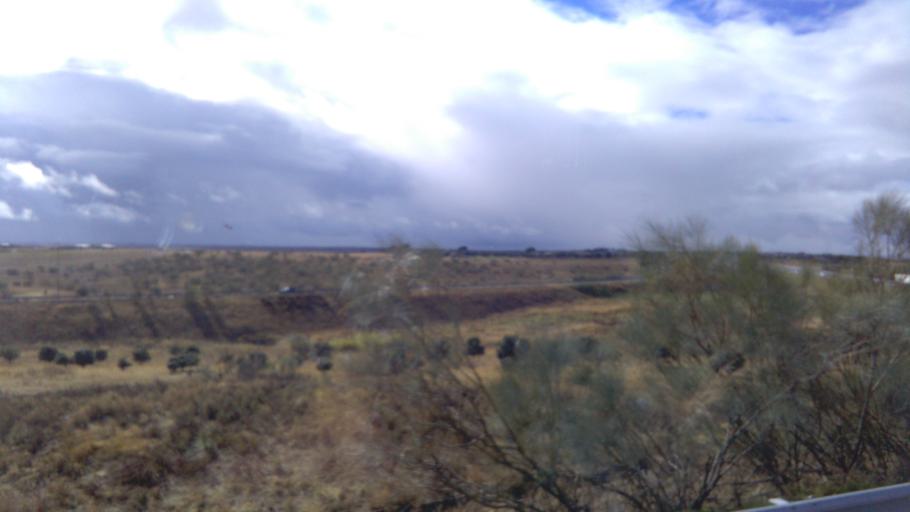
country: ES
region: Madrid
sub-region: Provincia de Madrid
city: Navalcarnero
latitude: 40.2676
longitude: -4.0359
